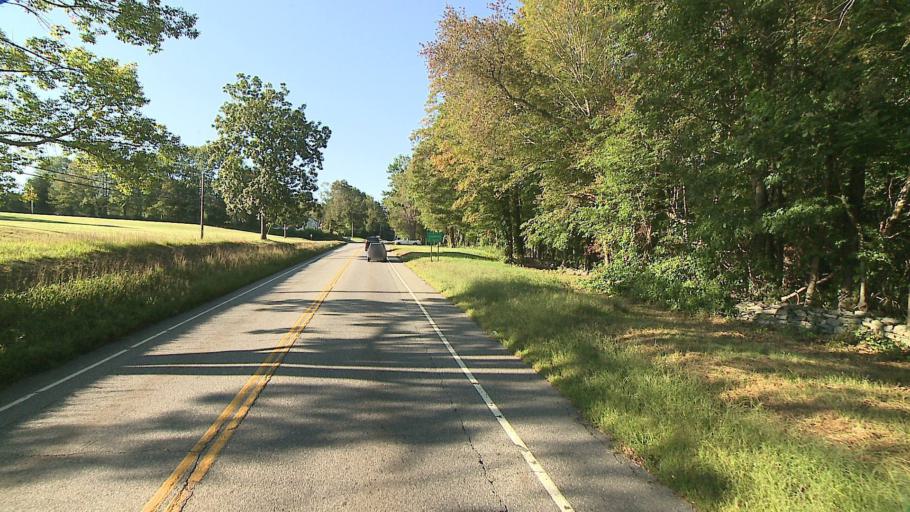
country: US
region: Connecticut
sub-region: Windham County
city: Plainfield
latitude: 41.6970
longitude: -71.9089
